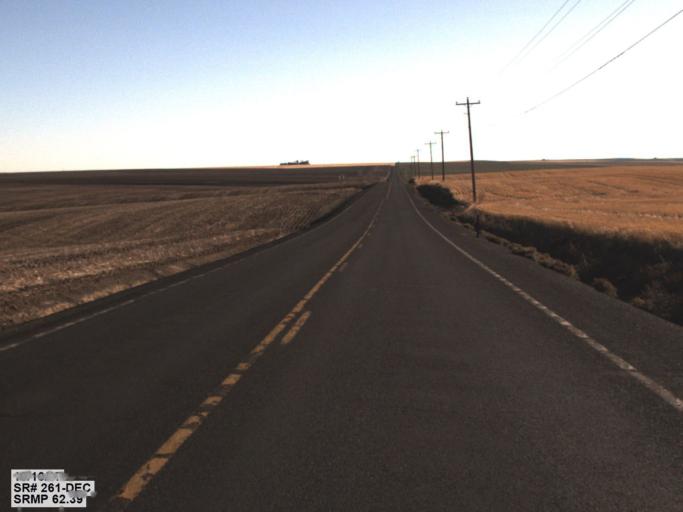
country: US
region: Washington
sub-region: Adams County
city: Ritzville
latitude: 47.1106
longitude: -118.3656
